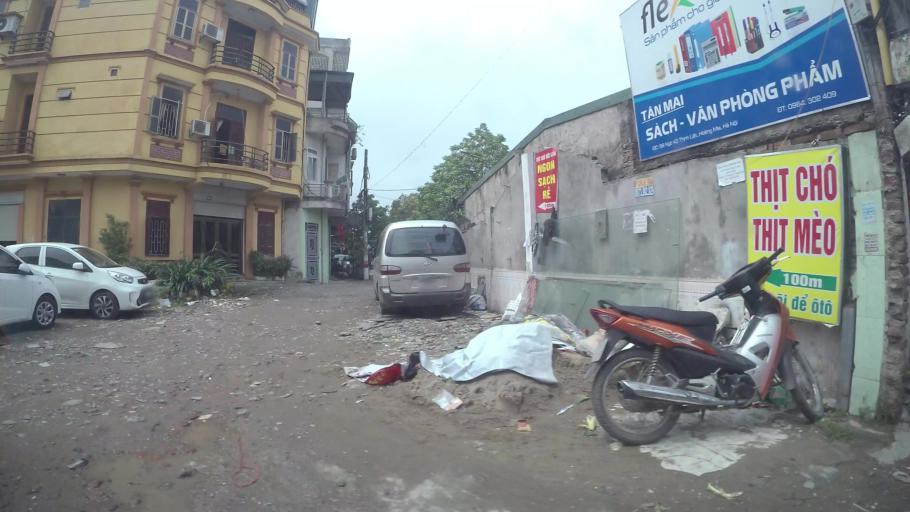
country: VN
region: Ha Noi
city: Van Dien
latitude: 20.9727
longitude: 105.8464
